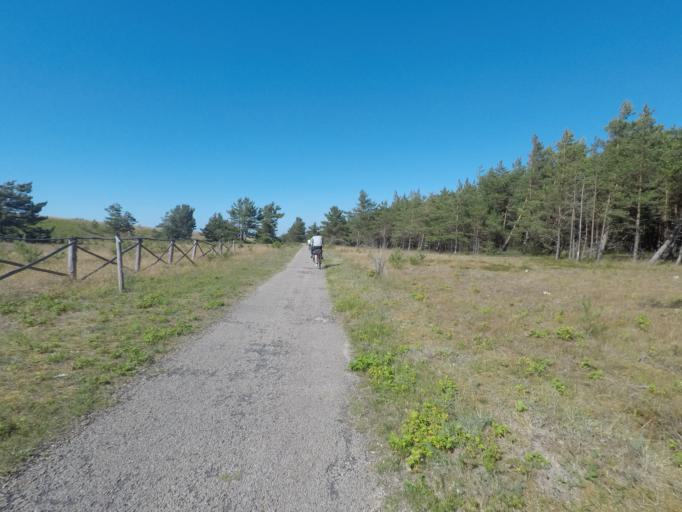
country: LT
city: Neringa
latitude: 55.4942
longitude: 21.0872
